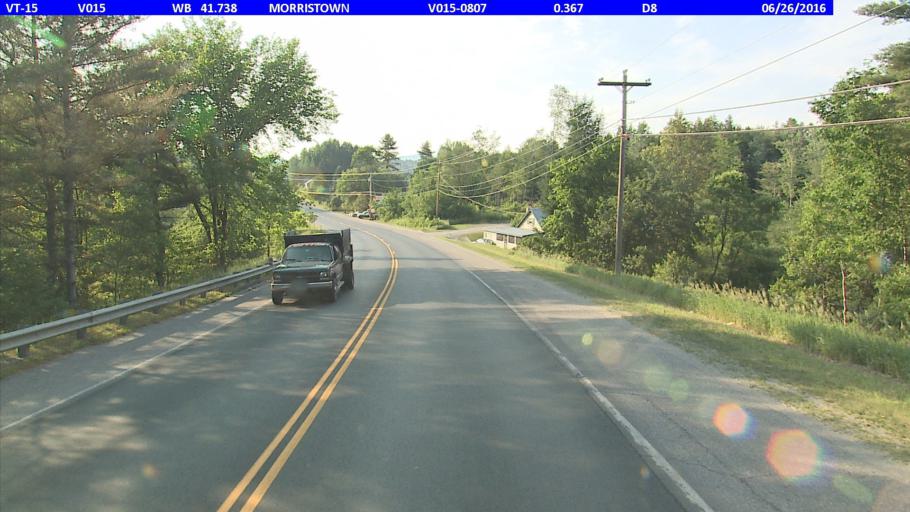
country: US
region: Vermont
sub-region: Lamoille County
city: Morrisville
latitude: 44.5815
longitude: -72.5980
